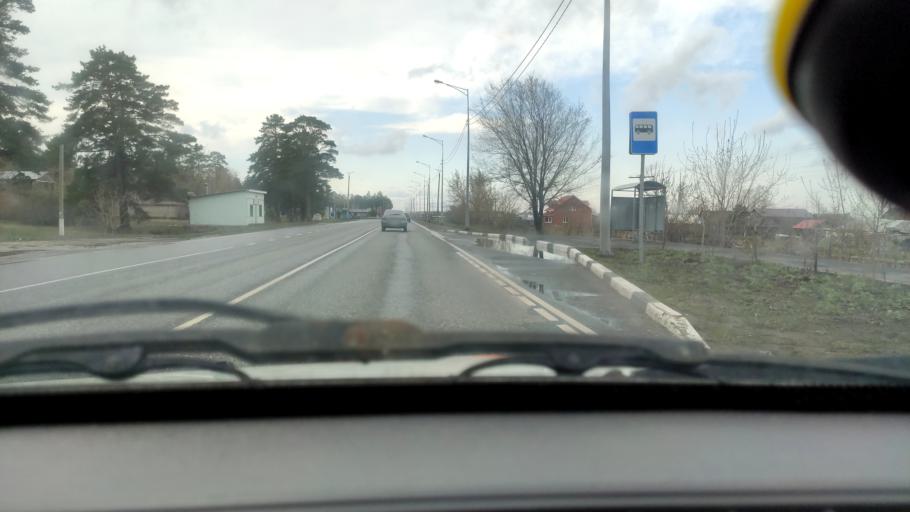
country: RU
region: Samara
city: Povolzhskiy
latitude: 53.5862
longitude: 49.5727
